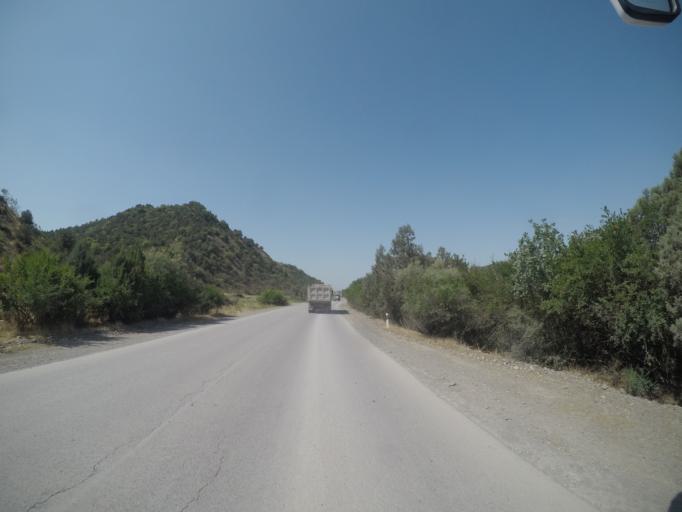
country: AZ
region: Agdas
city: Agdas
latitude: 40.7311
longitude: 47.5719
